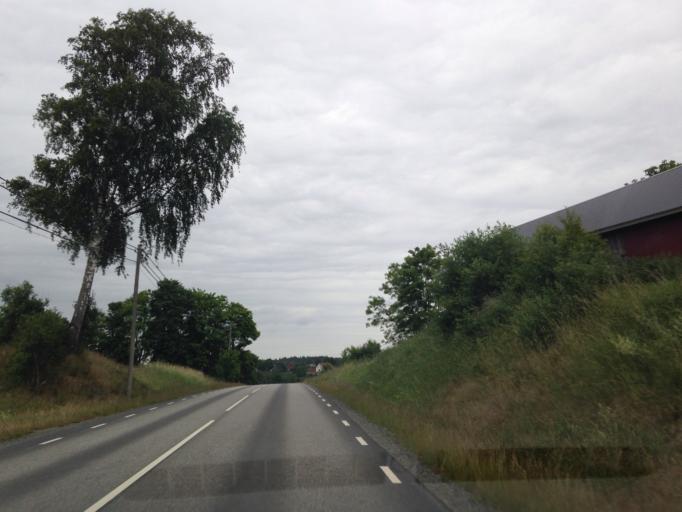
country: SE
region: Vaestra Goetaland
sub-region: Marks Kommun
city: Bua
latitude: 57.4993
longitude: 12.5412
